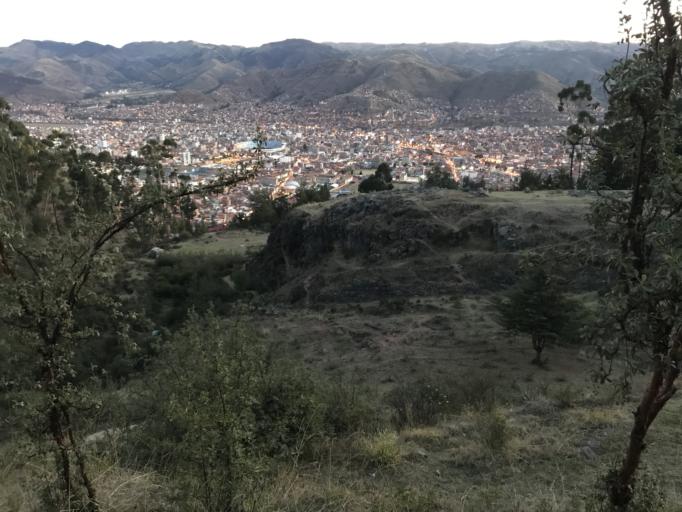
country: PE
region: Cusco
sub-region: Provincia de Cusco
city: Cusco
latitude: -13.5094
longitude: -71.9715
